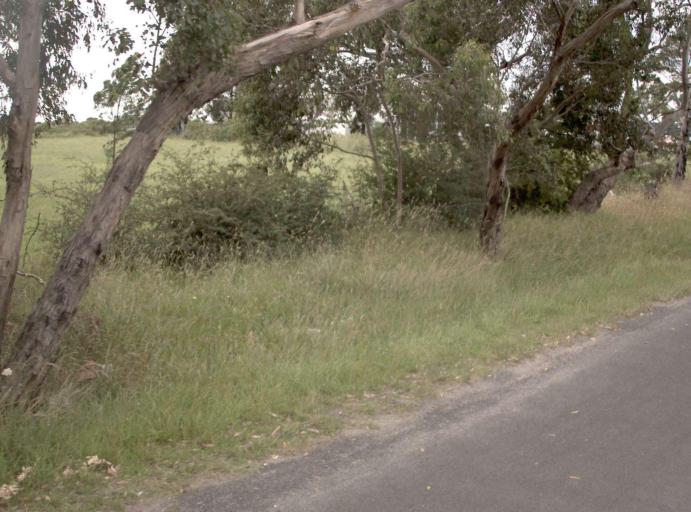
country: AU
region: Victoria
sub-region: Casey
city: Cranbourne
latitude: -38.0938
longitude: 145.2817
